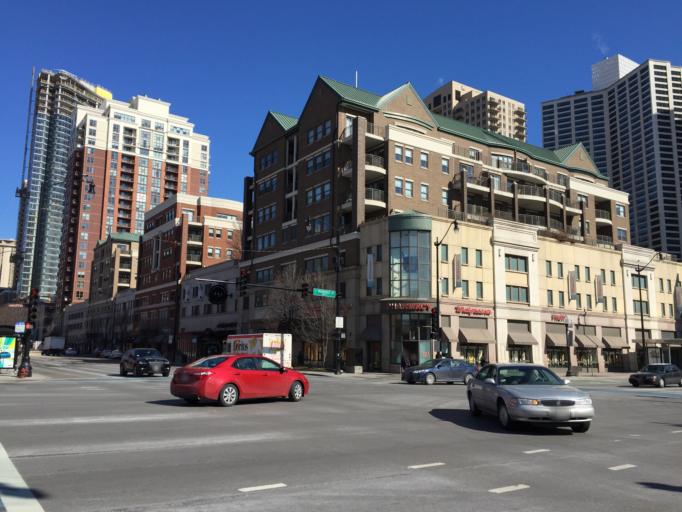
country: US
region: Illinois
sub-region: Cook County
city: Chicago
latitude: 41.8673
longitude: -87.6276
